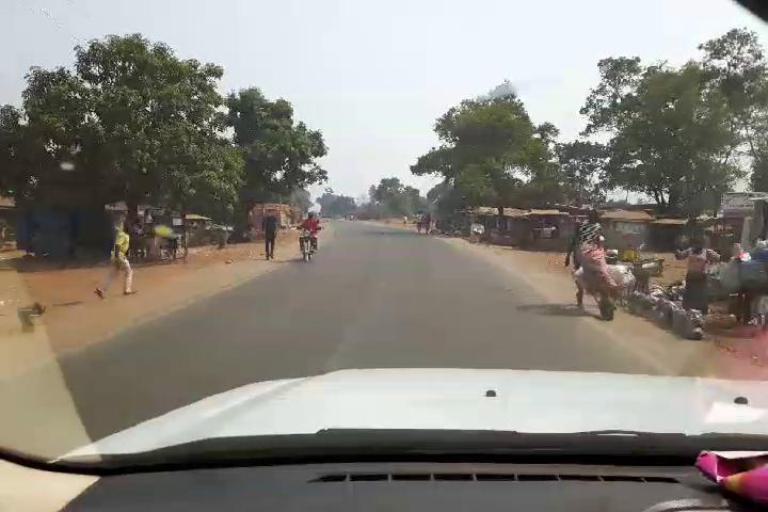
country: SL
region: Western Area
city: Waterloo
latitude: 8.3184
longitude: -13.0733
